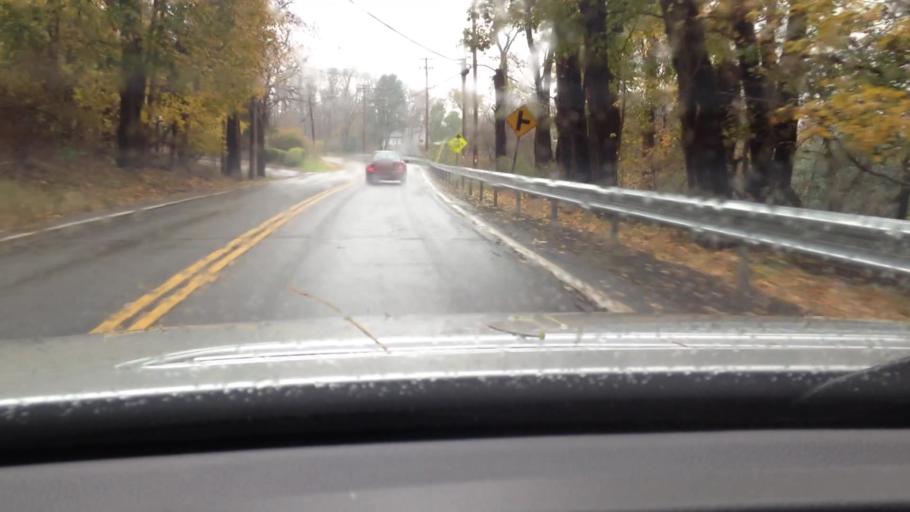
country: US
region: New York
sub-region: Dutchess County
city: Beacon
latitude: 41.4811
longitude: -73.9711
